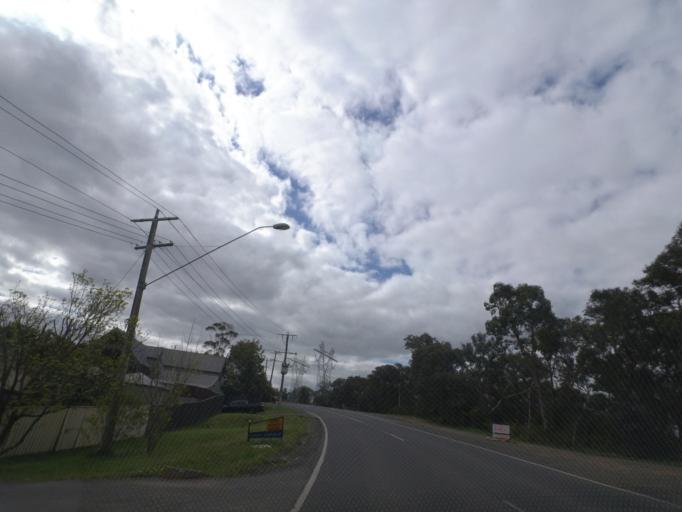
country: AU
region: Victoria
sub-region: Nillumbik
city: Diamond Creek
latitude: -37.6664
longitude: 145.1641
